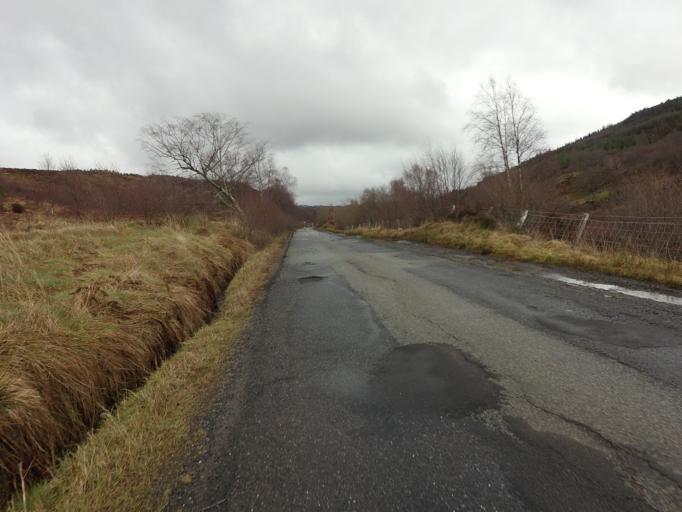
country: GB
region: Scotland
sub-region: West Dunbartonshire
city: Balloch
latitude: 56.2448
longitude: -4.5760
